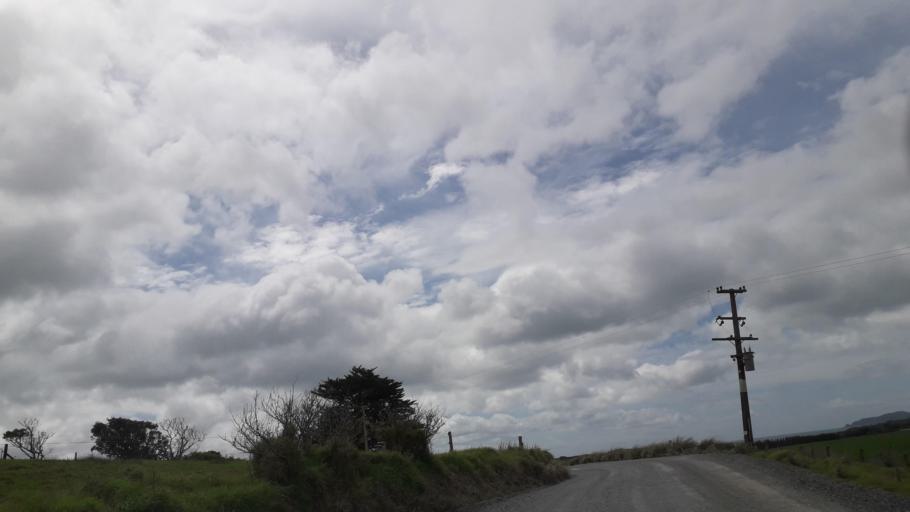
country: NZ
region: Northland
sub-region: Far North District
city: Taipa
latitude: -35.0020
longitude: 173.4309
